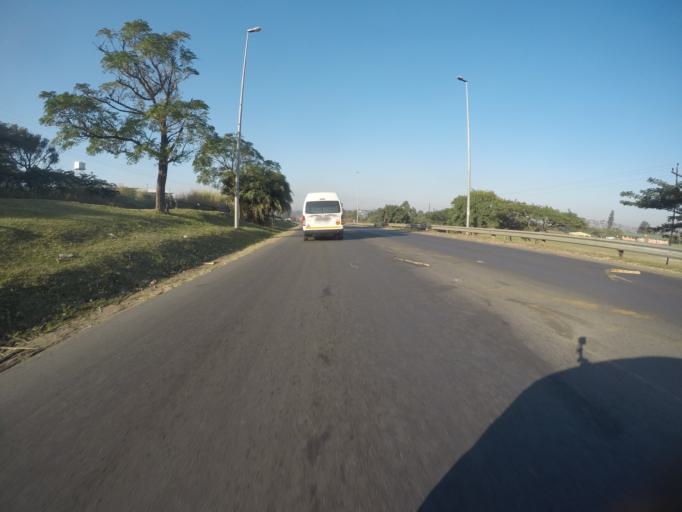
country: ZA
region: KwaZulu-Natal
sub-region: iLembe District Municipality
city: Stanger
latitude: -29.3895
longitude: 31.2508
